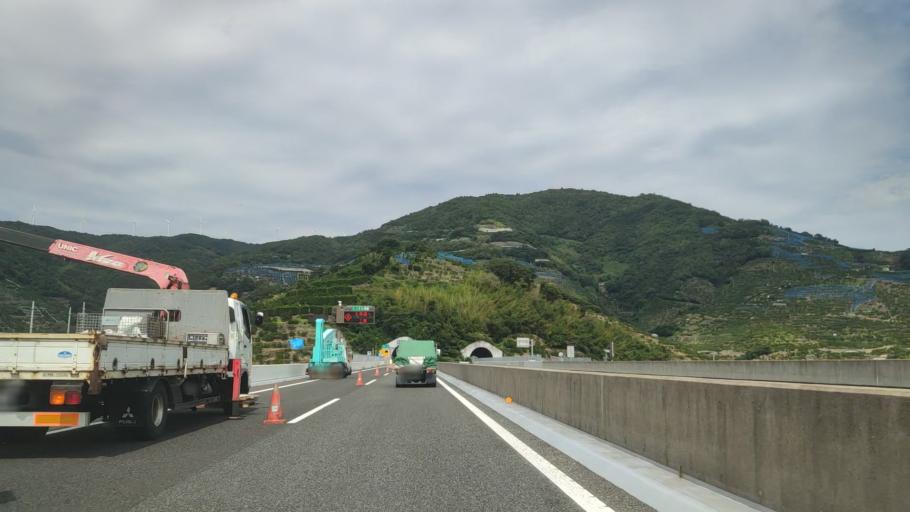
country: JP
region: Wakayama
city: Kainan
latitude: 34.0747
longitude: 135.2007
